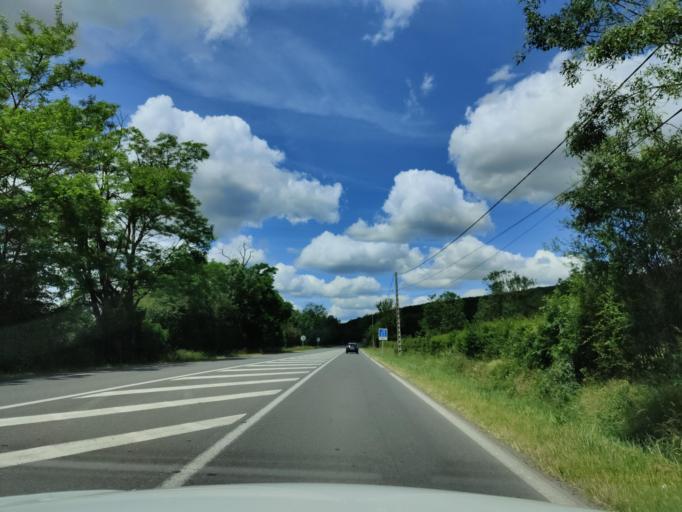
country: FR
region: Centre
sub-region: Departement du Cher
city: Orval
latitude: 46.7391
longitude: 2.4805
